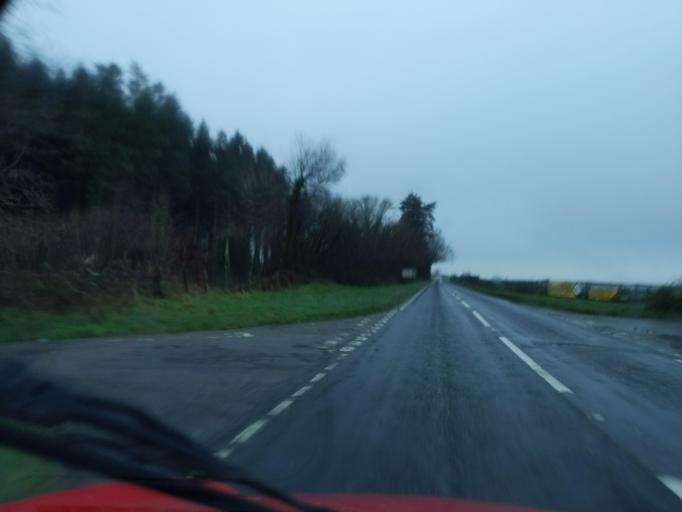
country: GB
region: England
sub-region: Cornwall
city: South Hill
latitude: 50.5360
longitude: -4.3348
